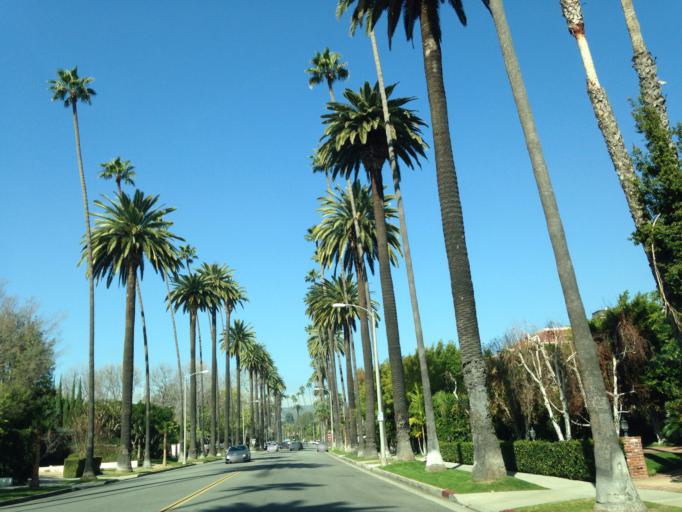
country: US
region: California
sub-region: Los Angeles County
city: Beverly Hills
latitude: 34.0743
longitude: -118.4044
